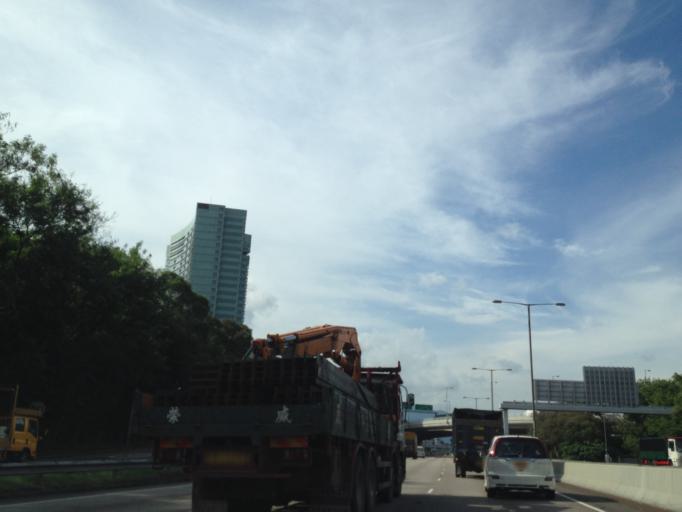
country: HK
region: Sha Tin
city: Sha Tin
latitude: 22.4088
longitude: 114.2117
